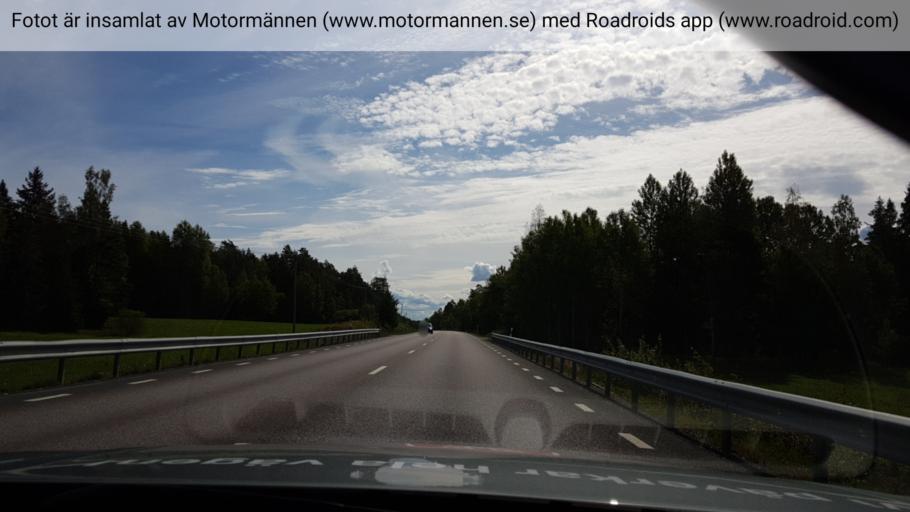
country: SE
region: Uppsala
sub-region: Osthammars Kommun
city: Bjorklinge
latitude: 59.9731
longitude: 17.3598
